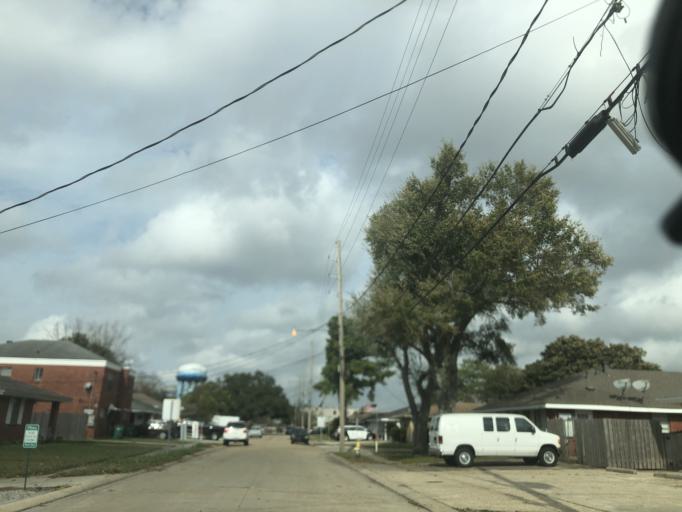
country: US
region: Louisiana
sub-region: Jefferson Parish
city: Metairie
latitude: 29.9928
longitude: -90.1576
